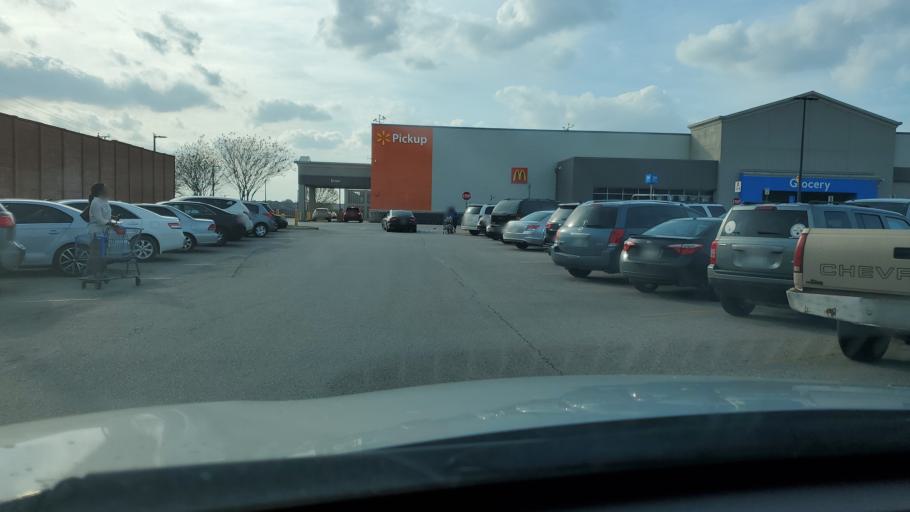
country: US
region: Texas
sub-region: Bell County
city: Harker Heights
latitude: 31.0689
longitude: -97.6735
